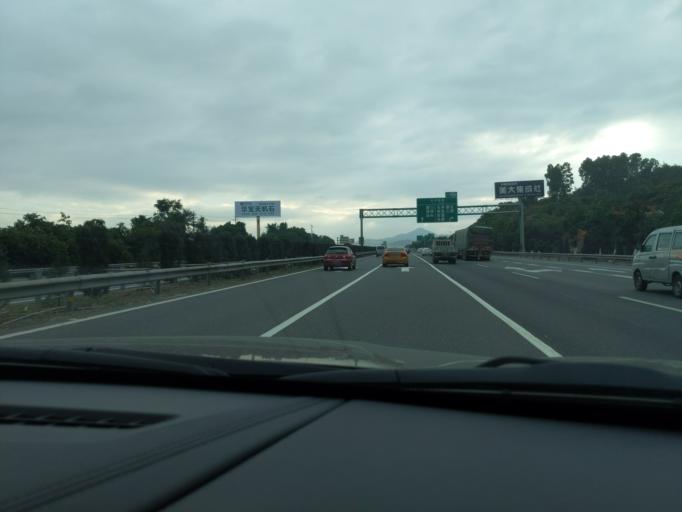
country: CN
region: Fujian
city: Anhai
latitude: 24.7226
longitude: 118.4060
